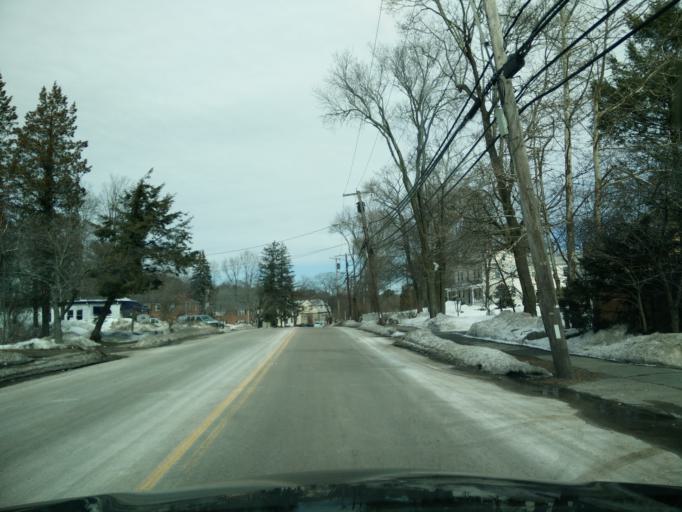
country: US
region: Massachusetts
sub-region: Norfolk County
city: Walpole
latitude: 42.1507
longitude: -71.2495
